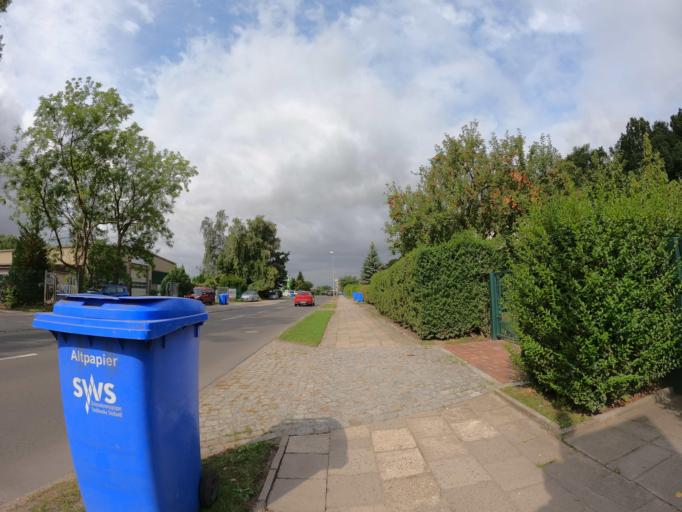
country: DE
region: Mecklenburg-Vorpommern
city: Stralsund
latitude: 54.3134
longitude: 13.0609
